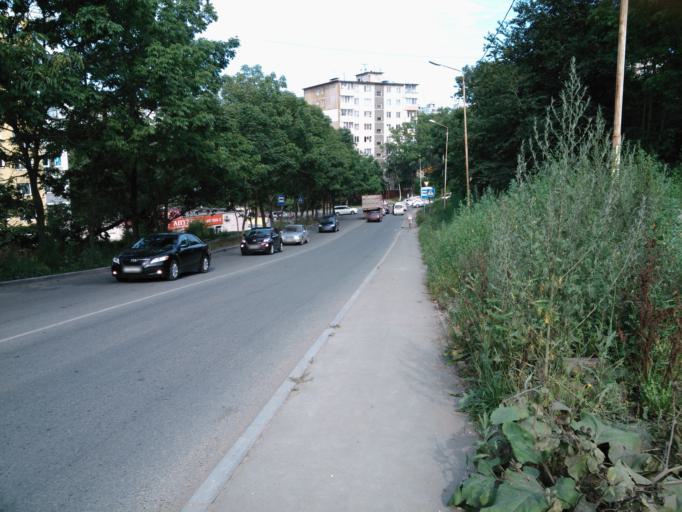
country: RU
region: Primorskiy
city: Vladivostok
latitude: 43.0913
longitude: 131.9650
